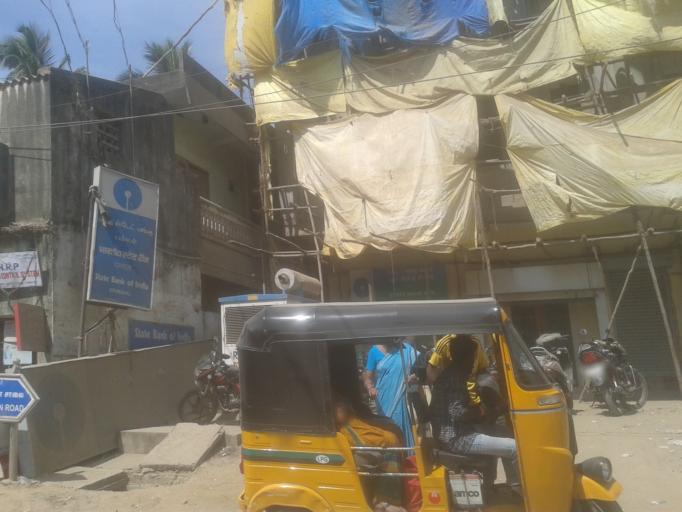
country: IN
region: Tamil Nadu
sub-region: Kancheepuram
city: Pallavaram
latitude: 12.9751
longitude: 80.1353
